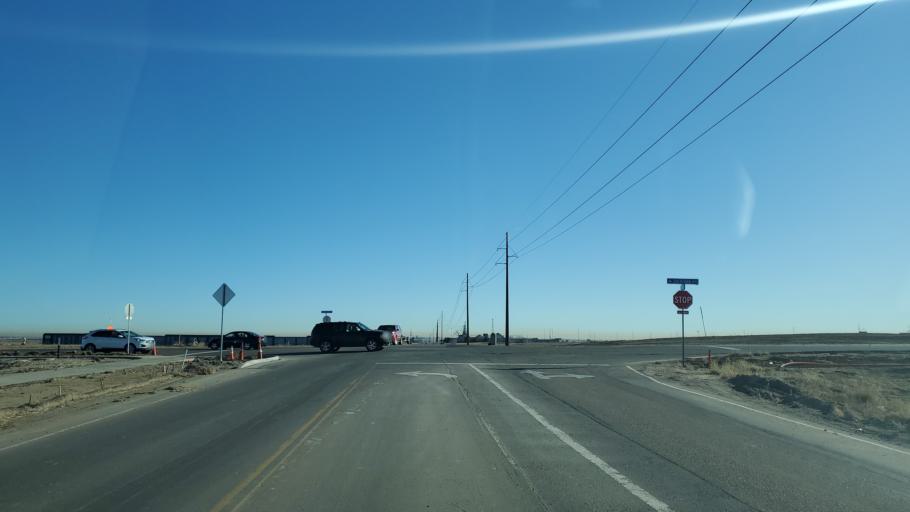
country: US
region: Colorado
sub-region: Boulder County
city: Erie
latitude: 39.9867
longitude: -105.0185
